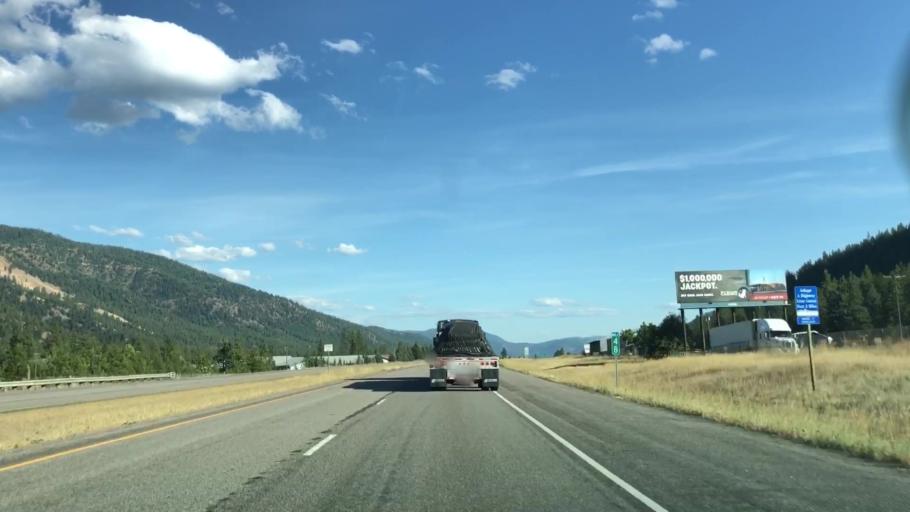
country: US
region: Montana
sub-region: Mineral County
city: Superior
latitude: 47.1888
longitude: -114.8835
